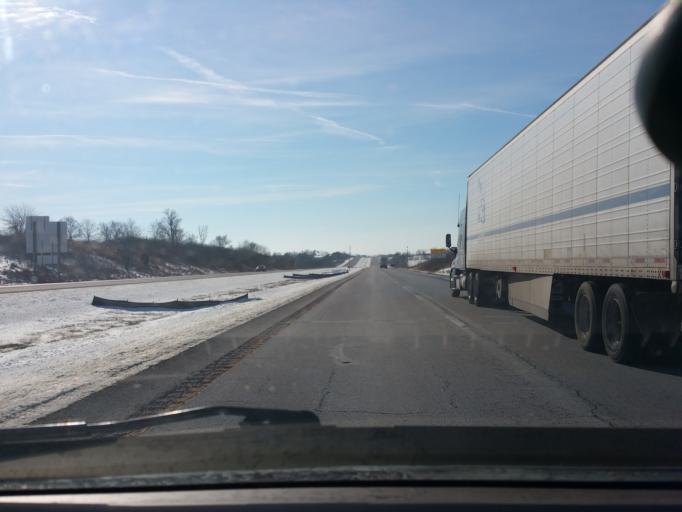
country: US
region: Iowa
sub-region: Decatur County
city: Lamoni
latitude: 40.5613
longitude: -93.9503
